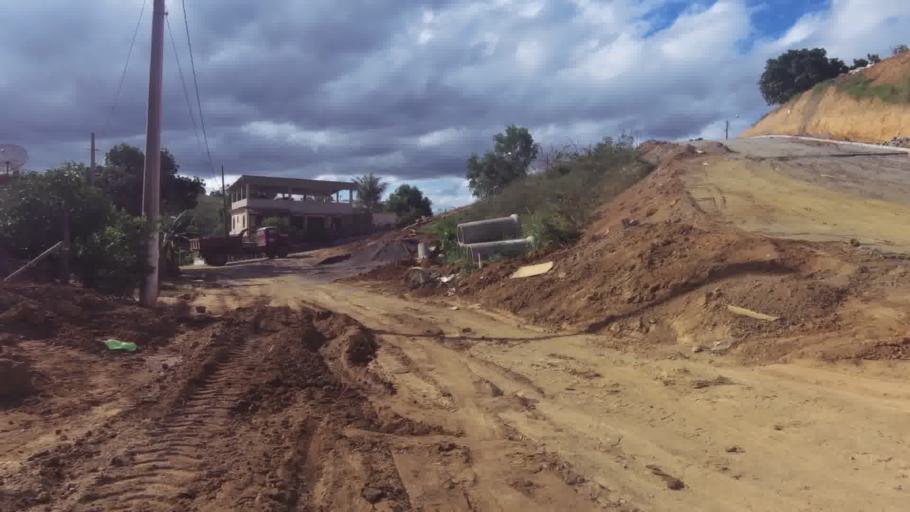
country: BR
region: Espirito Santo
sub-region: Marataizes
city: Marataizes
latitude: -21.1022
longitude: -41.0478
